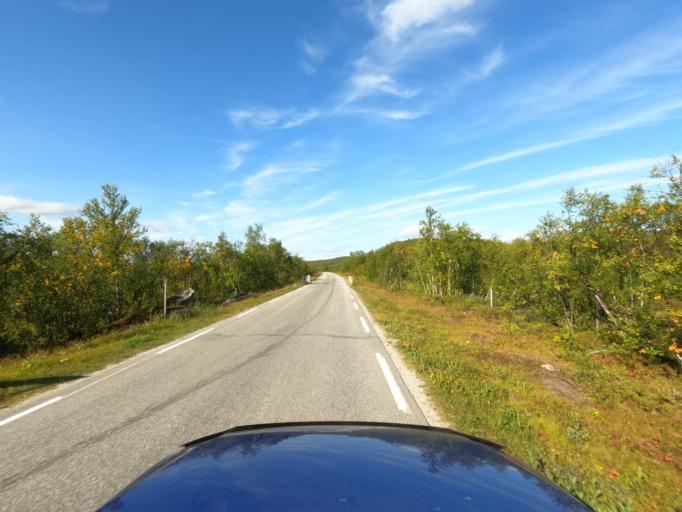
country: NO
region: Finnmark Fylke
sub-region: Porsanger
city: Lakselv
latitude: 69.7559
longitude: 25.2145
